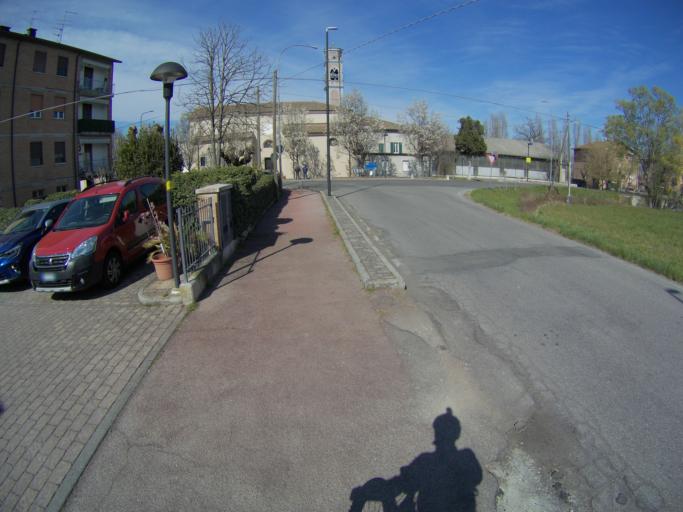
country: IT
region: Emilia-Romagna
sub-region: Provincia di Reggio Emilia
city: Massenzatico
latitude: 44.7047
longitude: 10.6800
